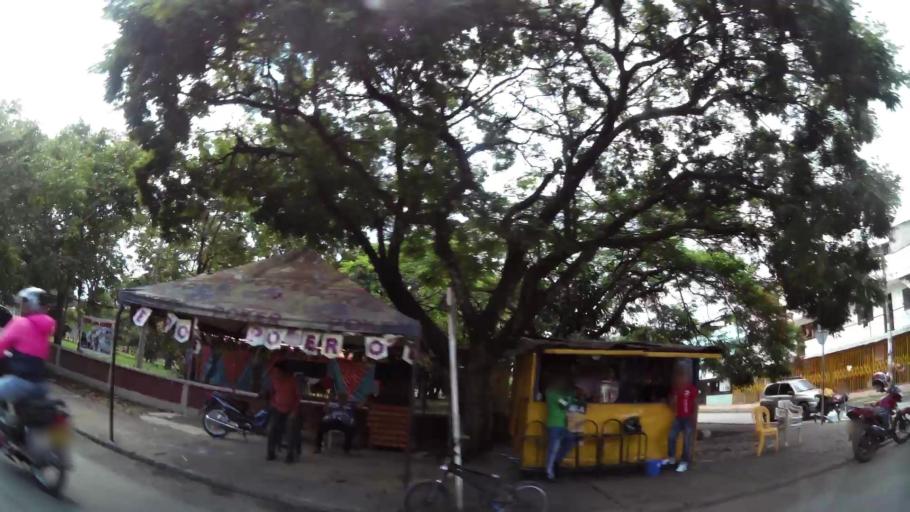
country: CO
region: Valle del Cauca
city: Cali
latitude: 3.4048
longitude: -76.5188
